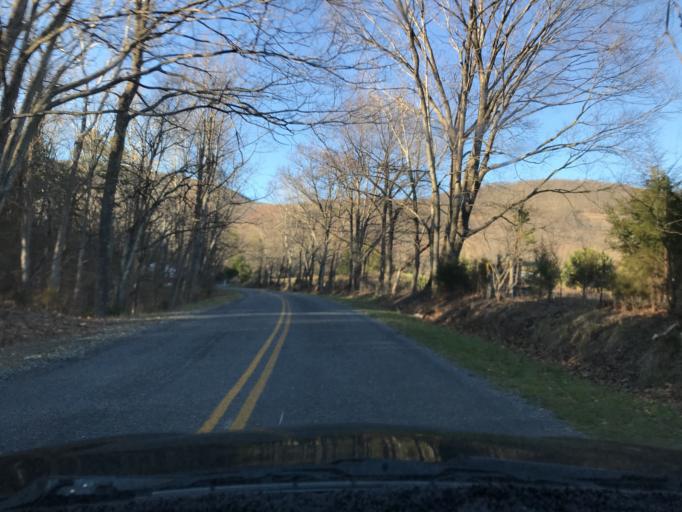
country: US
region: Virginia
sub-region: Botetourt County
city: Buchanan
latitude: 37.4668
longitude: -79.6584
